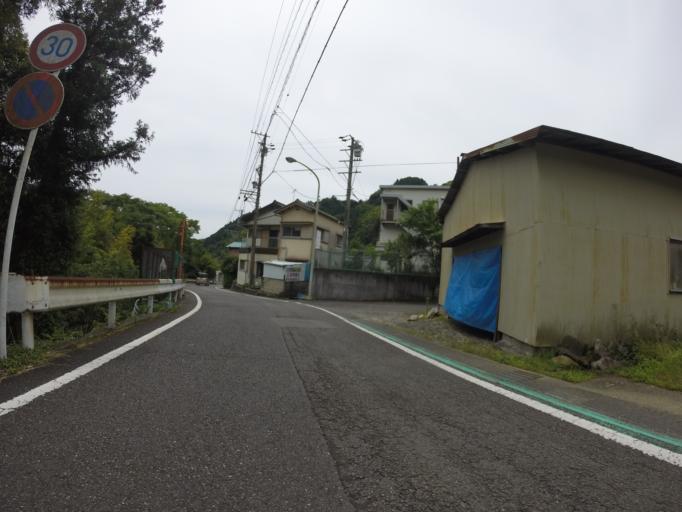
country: JP
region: Shizuoka
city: Shizuoka-shi
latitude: 35.0491
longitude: 138.4245
